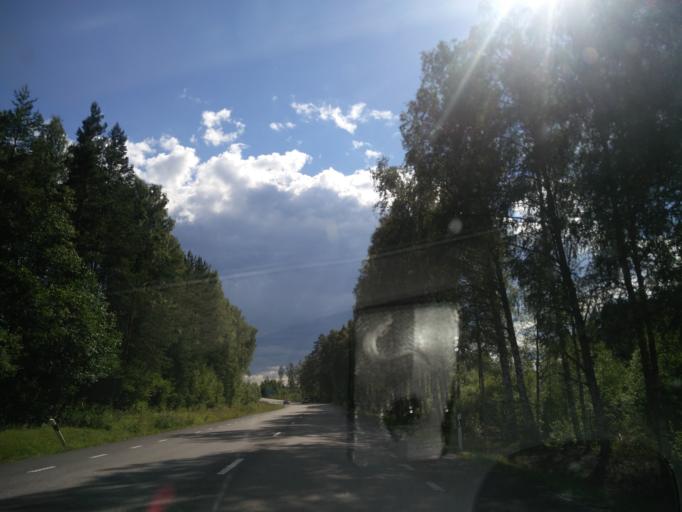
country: SE
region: OErebro
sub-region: Hallefors Kommun
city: Haellefors
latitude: 59.7537
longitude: 14.5102
